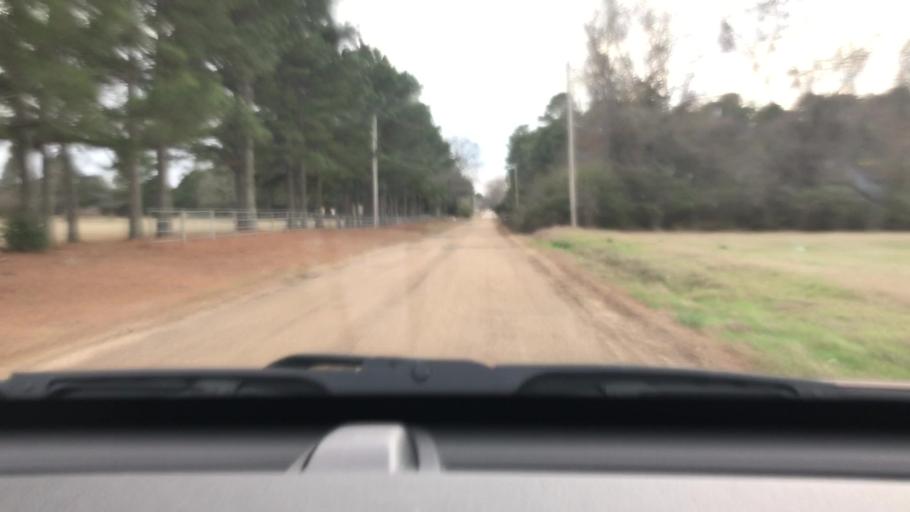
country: US
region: Arkansas
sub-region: Hempstead County
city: Hope
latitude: 33.6387
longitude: -93.5684
